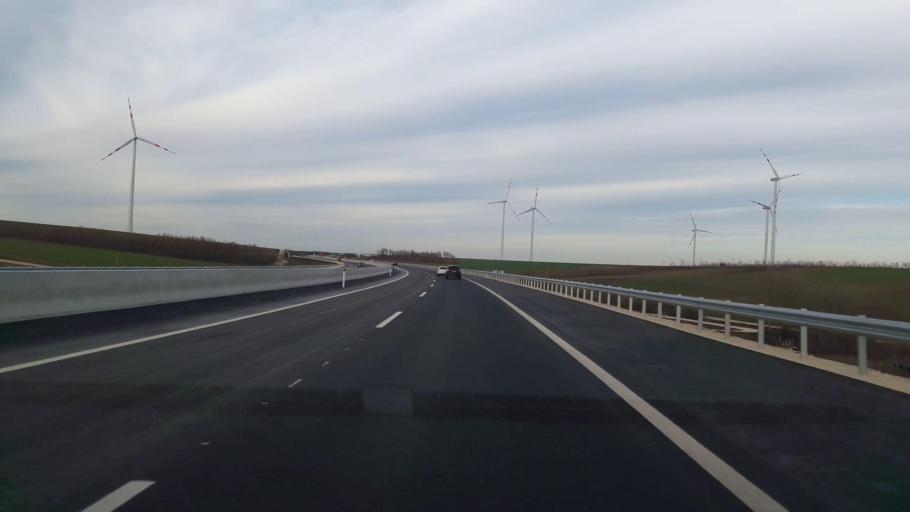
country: AT
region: Lower Austria
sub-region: Politischer Bezirk Mistelbach
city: Wilfersdorf
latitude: 48.6161
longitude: 16.6765
